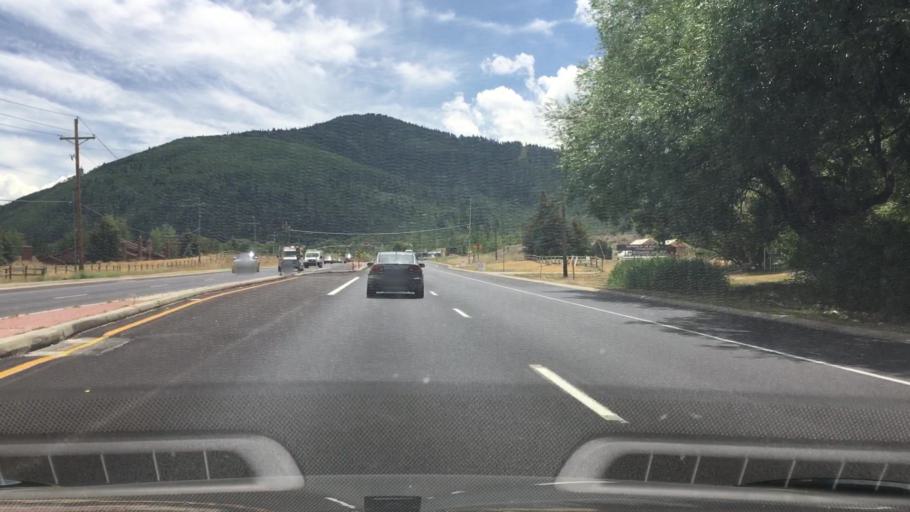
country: US
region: Utah
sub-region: Summit County
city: Snyderville
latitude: 40.6908
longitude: -111.5443
